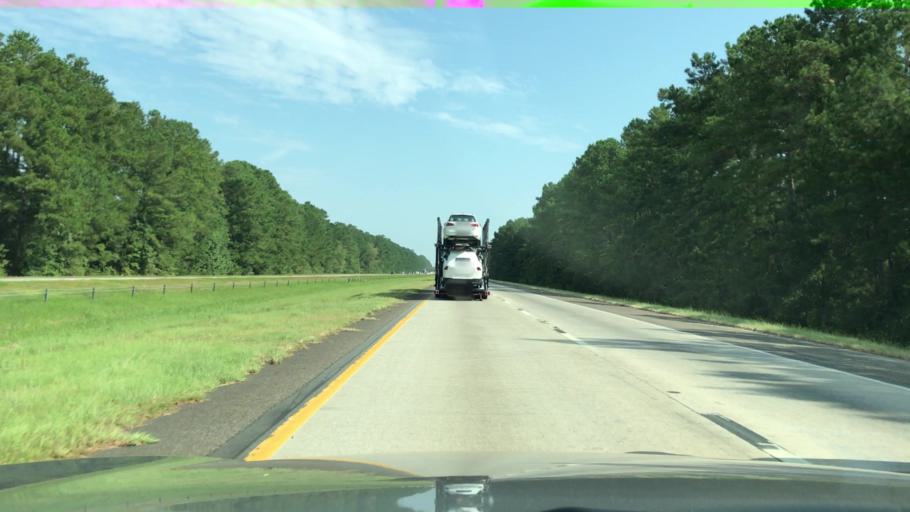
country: US
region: South Carolina
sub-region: Colleton County
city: Walterboro
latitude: 32.8294
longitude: -80.7468
